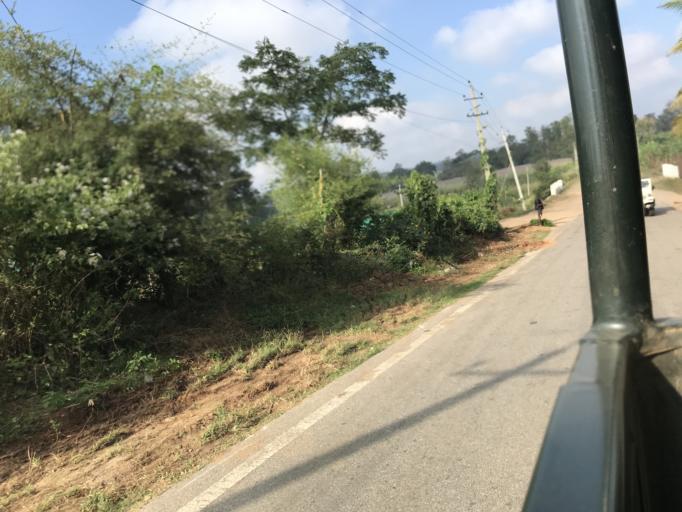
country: IN
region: Karnataka
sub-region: Mysore
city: Heggadadevankote
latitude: 11.9473
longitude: 76.2509
